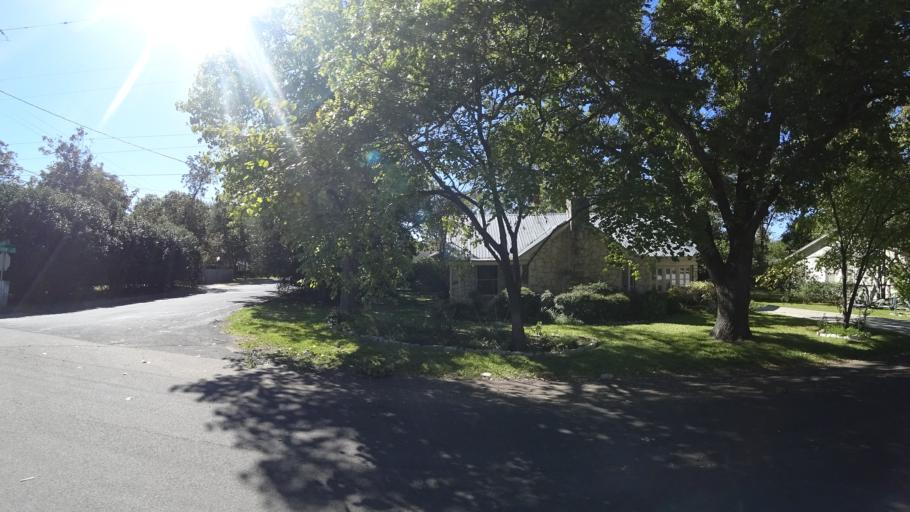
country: US
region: Texas
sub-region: Travis County
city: Austin
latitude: 30.3336
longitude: -97.7445
